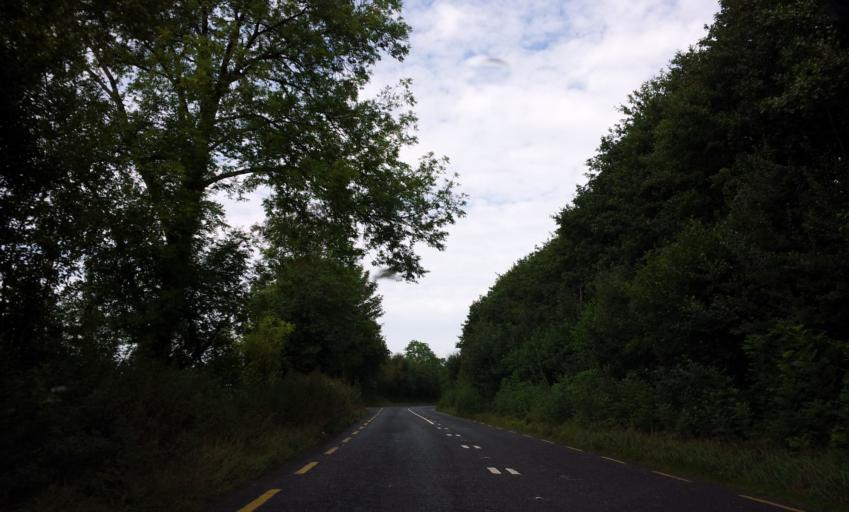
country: IE
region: Munster
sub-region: Ciarrai
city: Cill Airne
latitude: 52.0753
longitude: -9.6357
